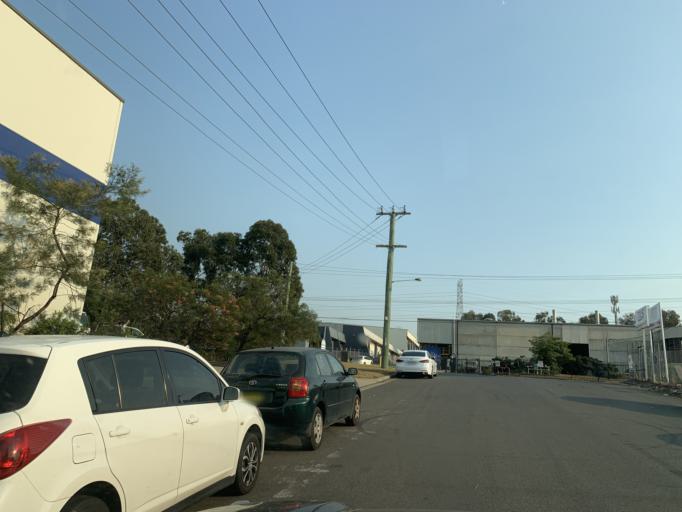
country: AU
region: New South Wales
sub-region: Fairfield
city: Horsley Park
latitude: -33.8386
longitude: 150.8857
